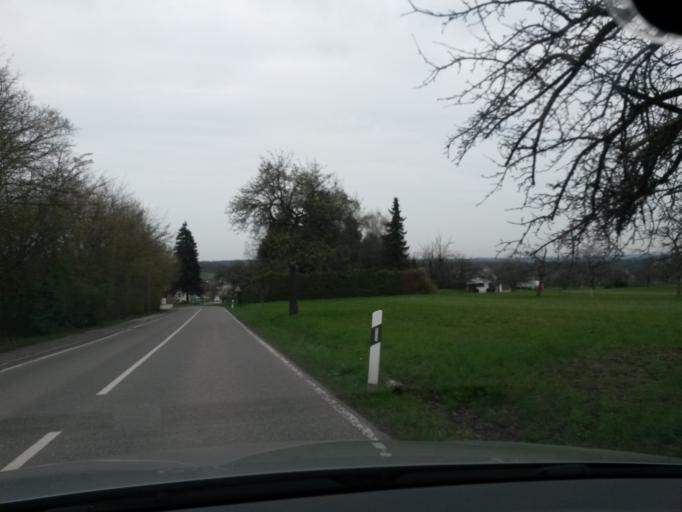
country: DE
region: Baden-Wuerttemberg
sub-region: Karlsruhe Region
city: Neuenburg
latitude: 48.8578
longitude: 8.5727
